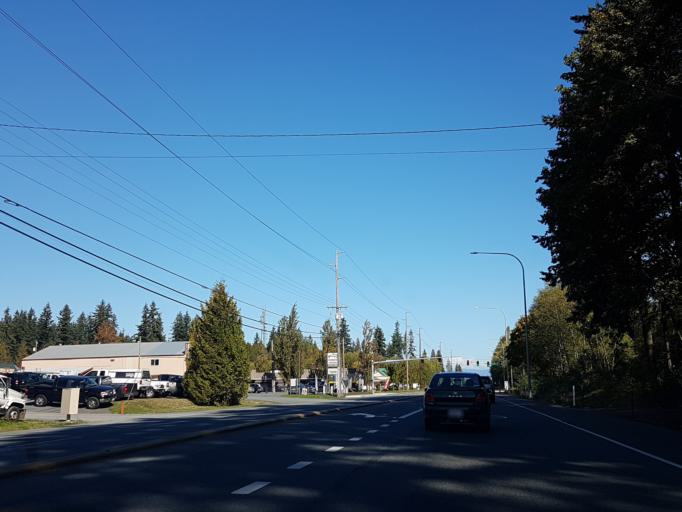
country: US
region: Washington
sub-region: Snohomish County
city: Clearview
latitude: 47.8361
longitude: -122.1247
